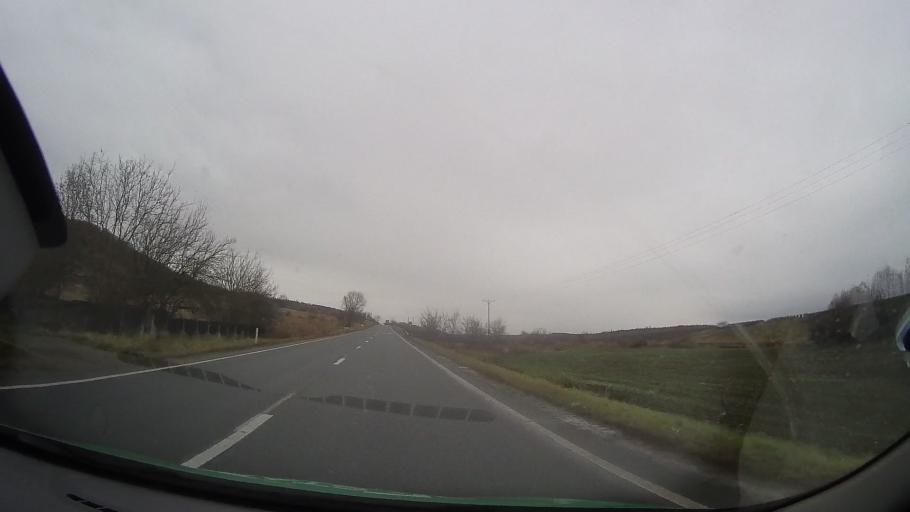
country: RO
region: Mures
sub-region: Comuna Breaza
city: Breaza
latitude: 46.7792
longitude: 24.6555
